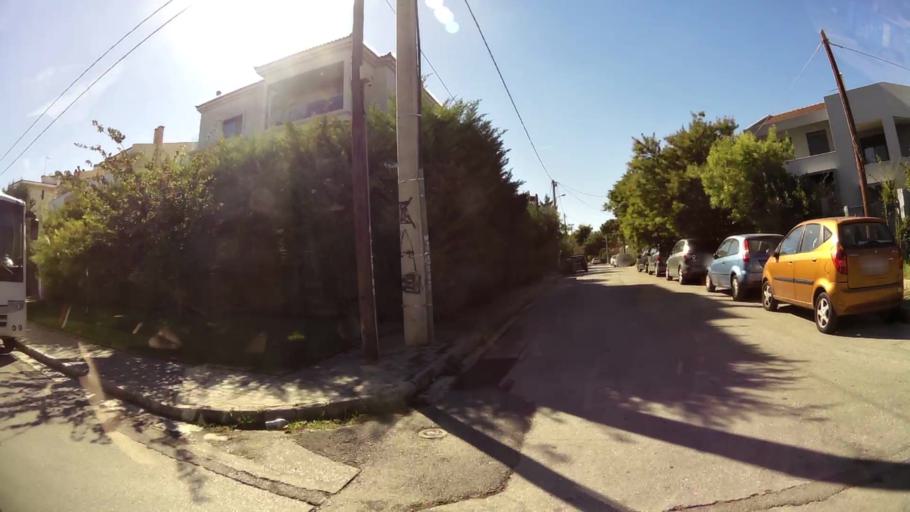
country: GR
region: Attica
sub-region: Nomarchia Athinas
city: Kifisia
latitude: 38.0893
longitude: 23.7934
